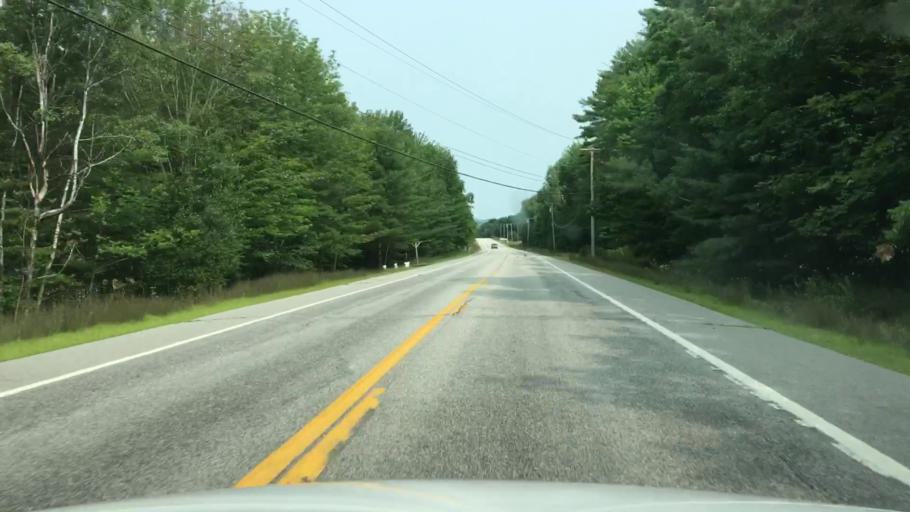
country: US
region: Maine
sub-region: Androscoggin County
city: Livermore Falls
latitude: 44.4314
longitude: -70.1466
